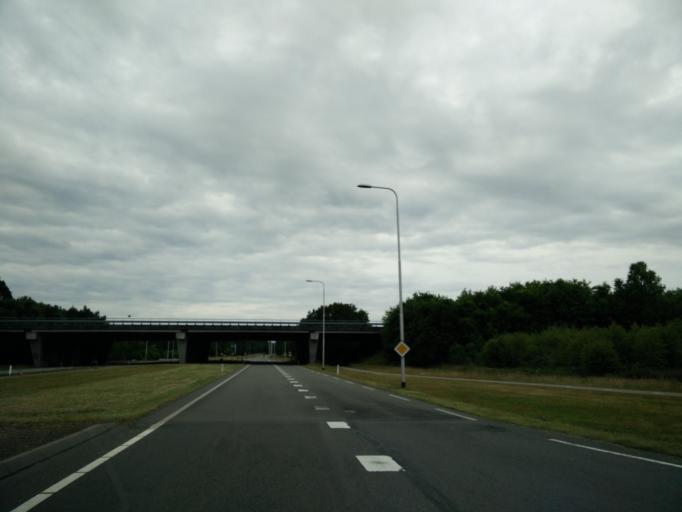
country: NL
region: Gelderland
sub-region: Gemeente Apeldoorn
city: Beekbergen
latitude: 52.1832
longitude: 5.9155
